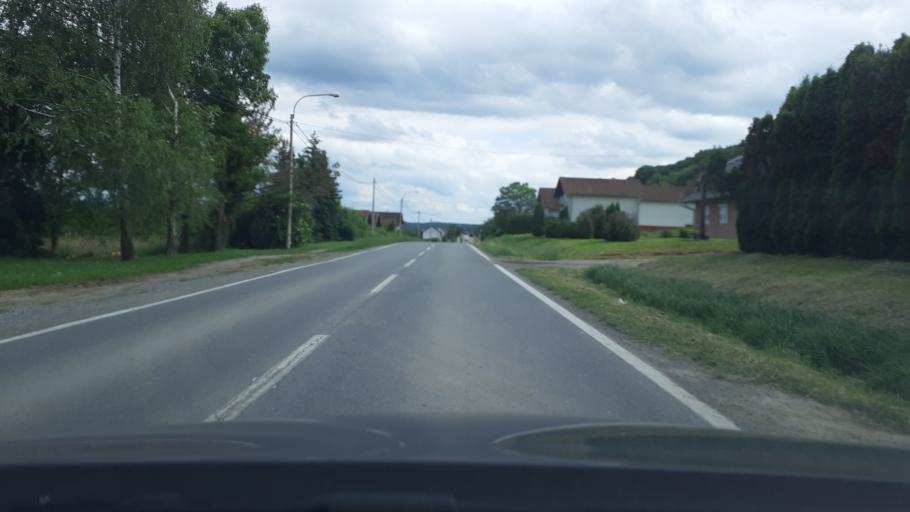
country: HR
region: Pozesko-Slavonska
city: Pleternica
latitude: 45.3037
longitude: 17.7900
